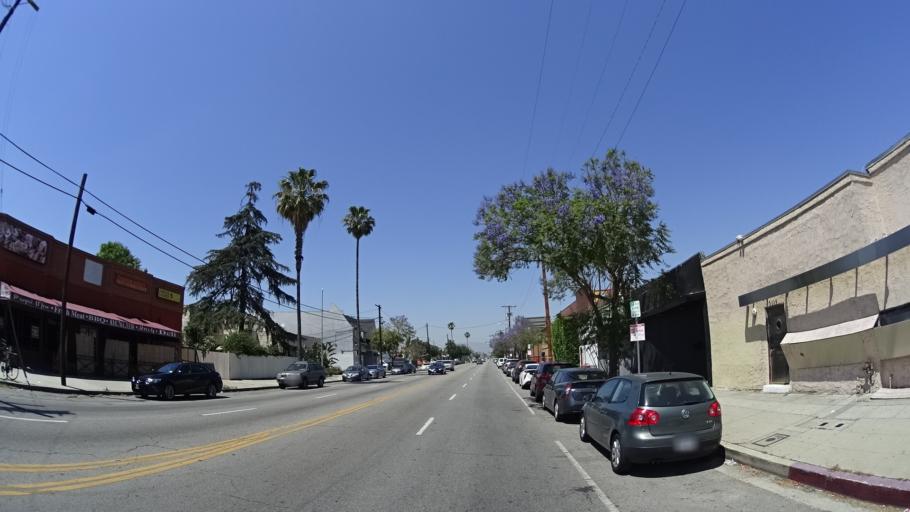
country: US
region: California
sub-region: Los Angeles County
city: North Hollywood
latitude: 34.1728
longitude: -118.3703
